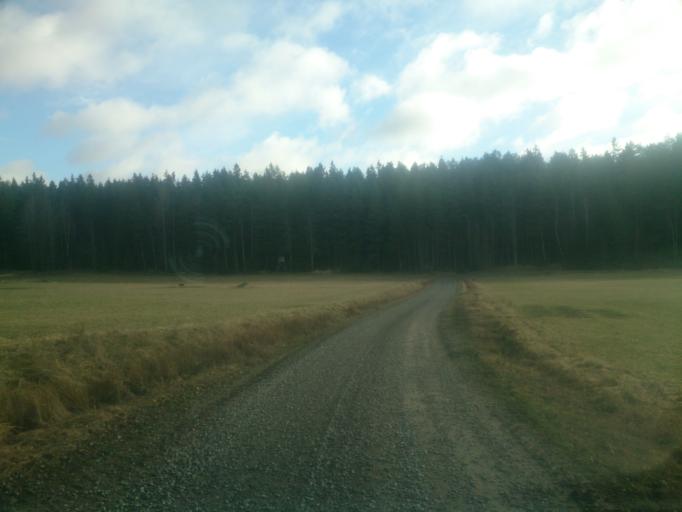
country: SE
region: OEstergoetland
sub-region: Atvidabergs Kommun
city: Atvidaberg
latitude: 58.2351
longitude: 16.1727
